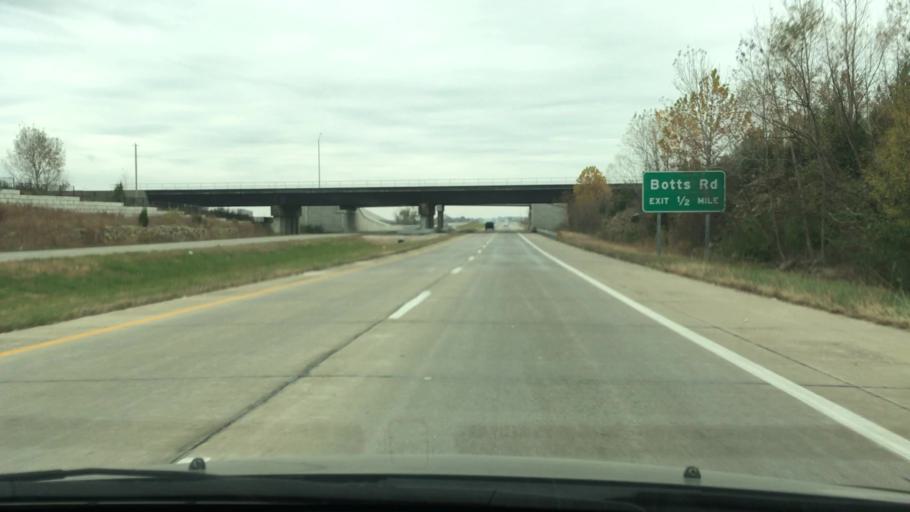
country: US
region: Missouri
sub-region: Jackson County
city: Grandview
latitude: 38.8592
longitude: -94.5611
